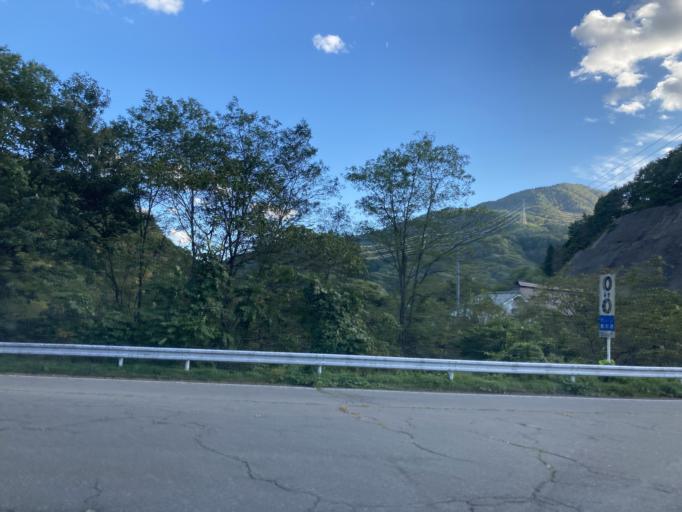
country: JP
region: Nagano
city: Ueda
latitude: 36.3931
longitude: 138.0972
